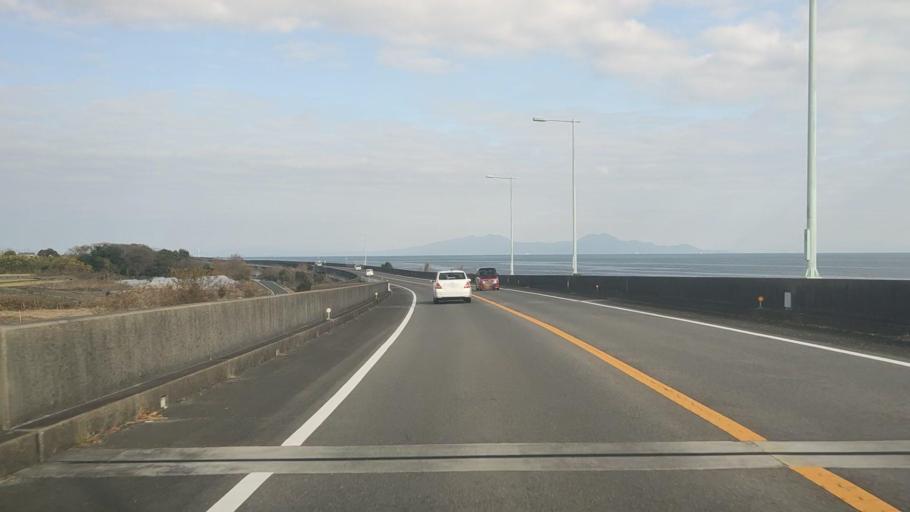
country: JP
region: Nagasaki
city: Shimabara
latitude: 32.7216
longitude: 130.3581
